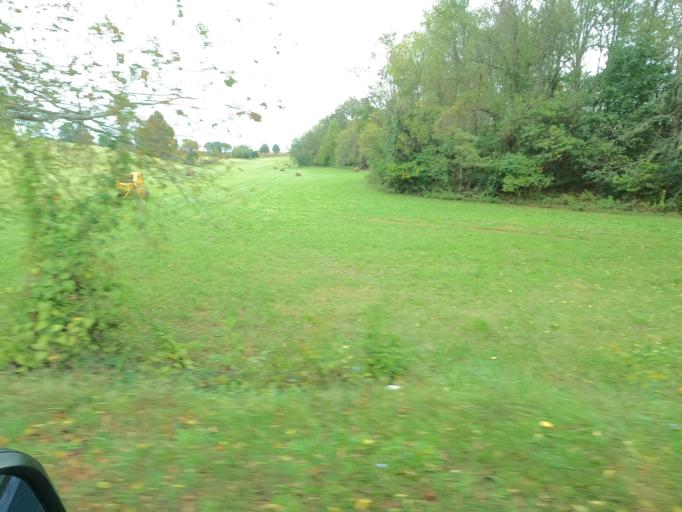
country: US
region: Tennessee
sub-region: Washington County
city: Jonesborough
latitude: 36.2361
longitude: -82.5824
